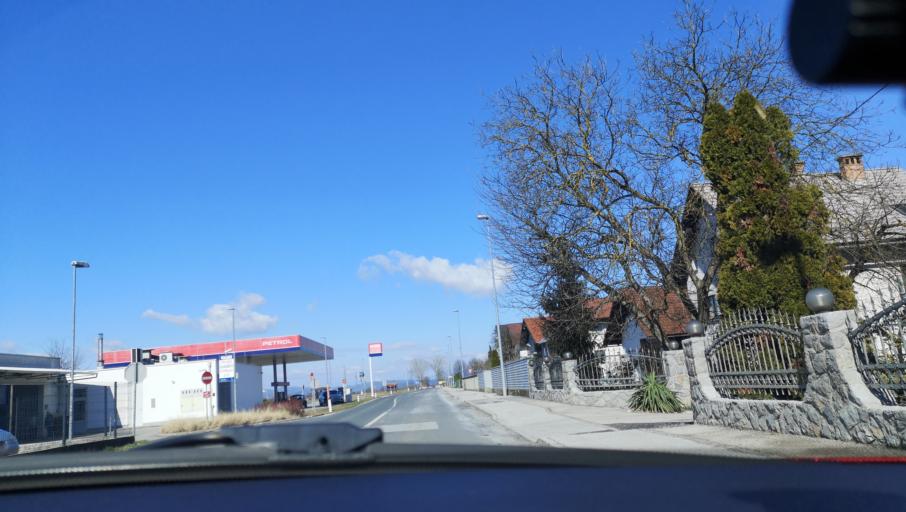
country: SI
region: Ig
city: Ig
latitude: 45.9624
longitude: 14.5306
